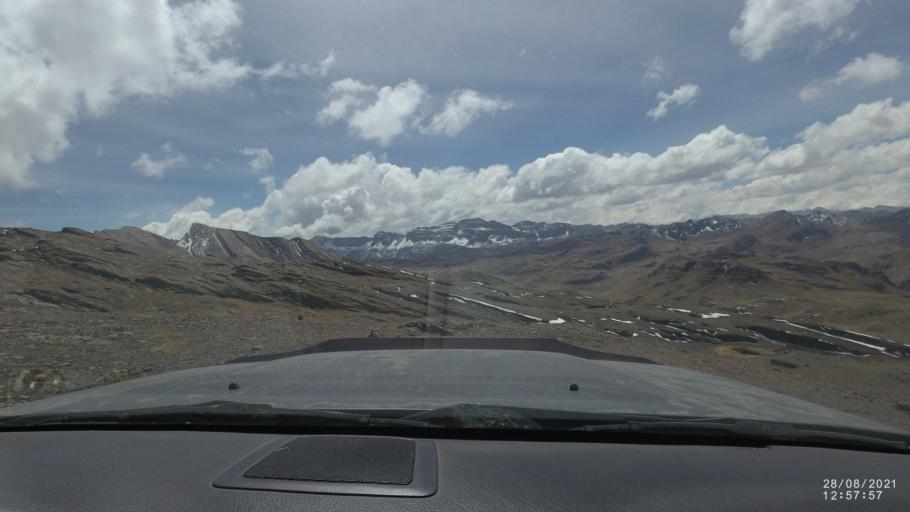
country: BO
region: Cochabamba
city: Sipe Sipe
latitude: -17.2835
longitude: -66.3857
